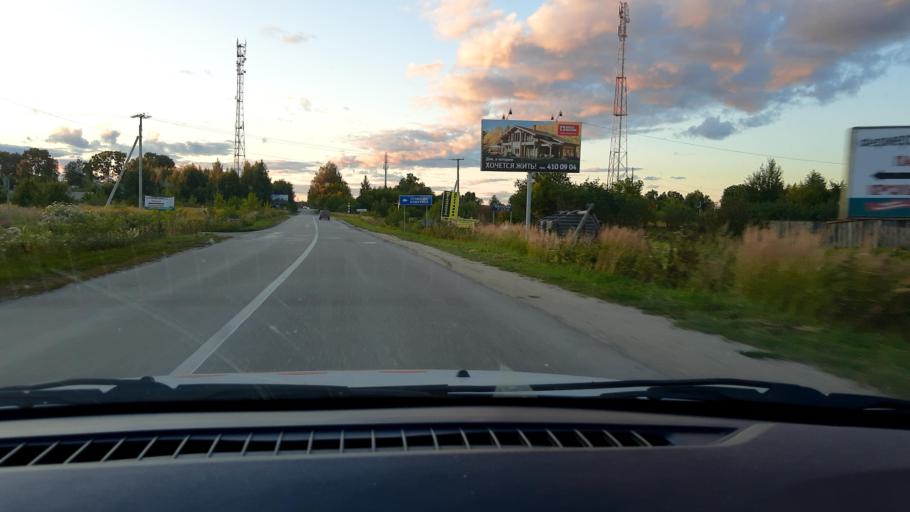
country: RU
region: Nizjnij Novgorod
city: Zavolzh'ye
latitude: 56.7119
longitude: 43.4161
